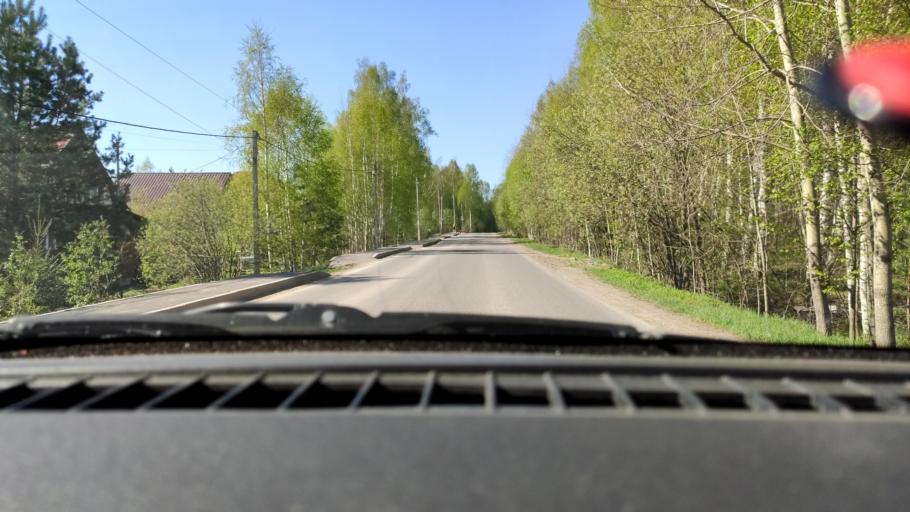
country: RU
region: Perm
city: Kondratovo
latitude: 58.0589
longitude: 56.0054
